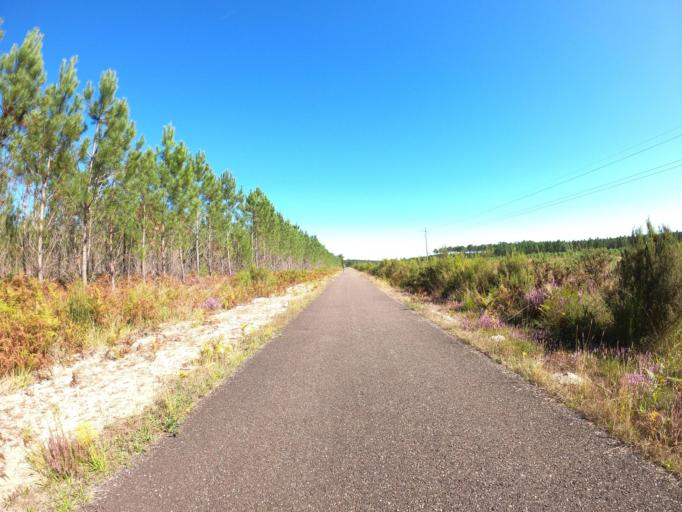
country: FR
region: Aquitaine
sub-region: Departement des Landes
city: Ychoux
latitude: 44.3403
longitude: -0.9762
